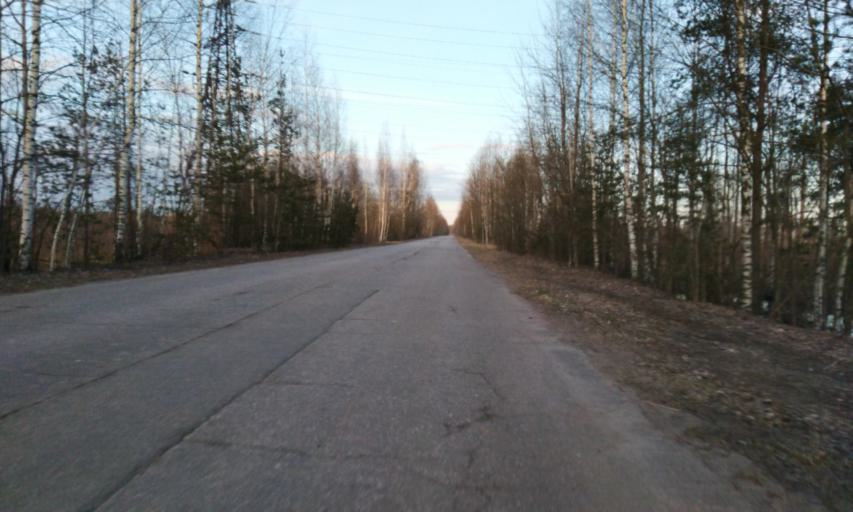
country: RU
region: Leningrad
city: Novoye Devyatkino
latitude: 60.0793
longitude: 30.4728
